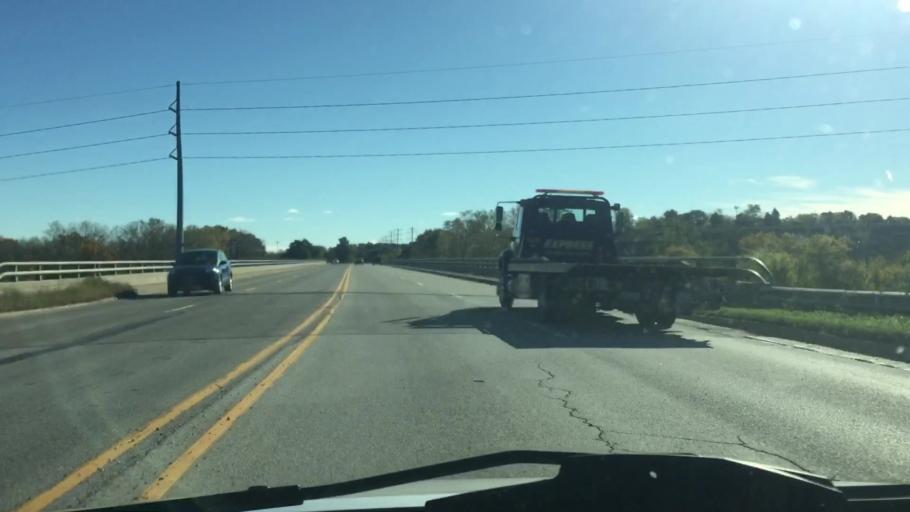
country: US
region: Wisconsin
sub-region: Waukesha County
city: Waukesha
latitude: 43.0381
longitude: -88.2135
